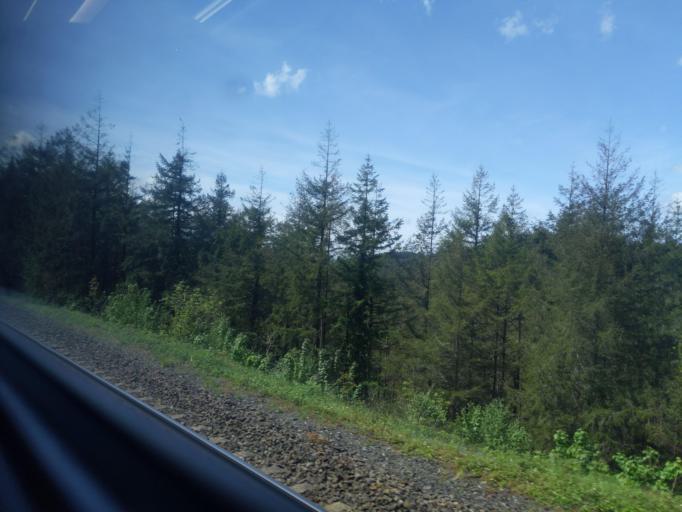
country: GB
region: England
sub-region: Cornwall
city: Liskeard
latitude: 50.4542
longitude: -4.5549
